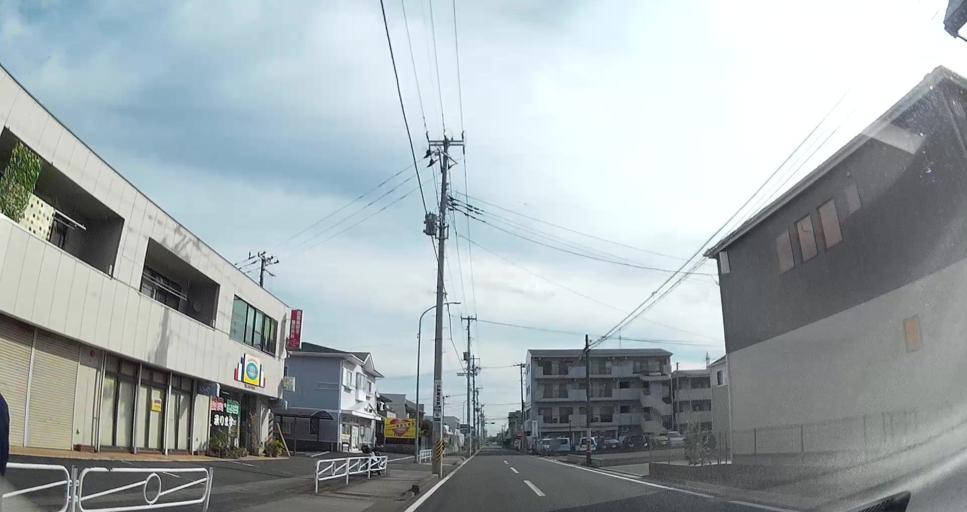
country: JP
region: Miyagi
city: Sendai
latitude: 38.2200
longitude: 140.9157
